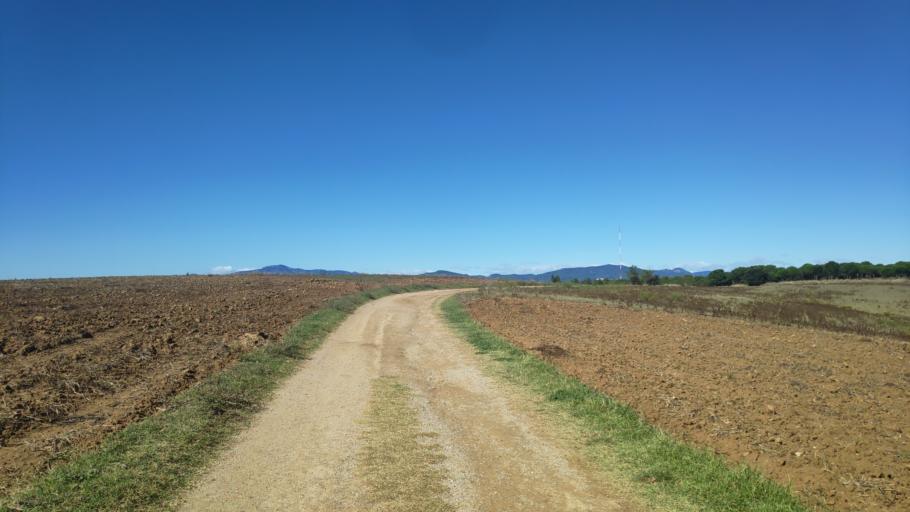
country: ES
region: Catalonia
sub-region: Provincia de Barcelona
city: Mollet del Valles
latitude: 41.5408
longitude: 2.2002
